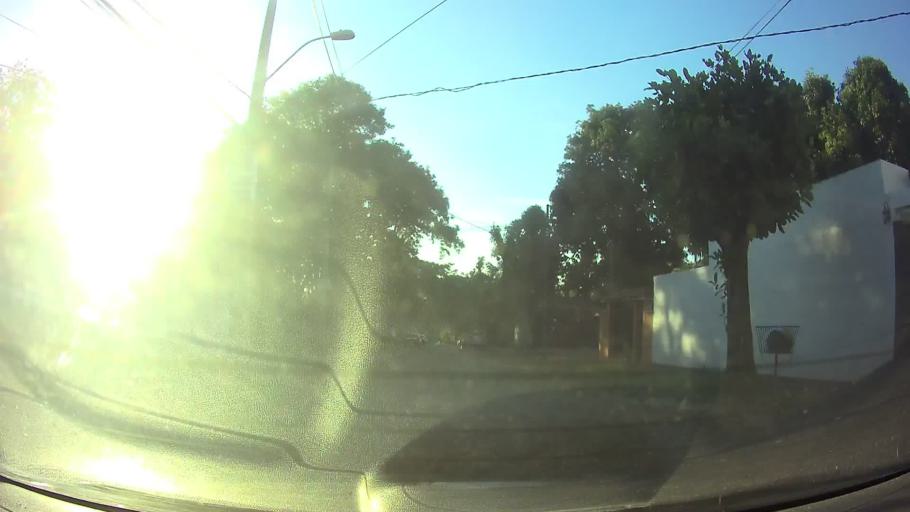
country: PY
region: Asuncion
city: Asuncion
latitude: -25.2826
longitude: -57.5847
